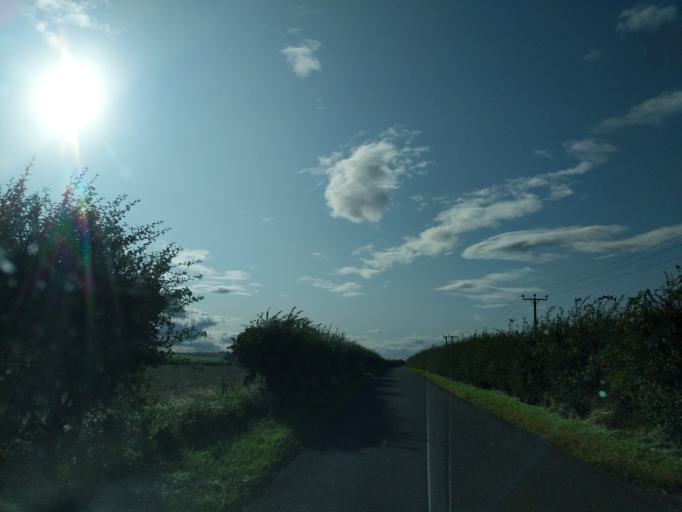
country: GB
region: Scotland
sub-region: East Lothian
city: Haddington
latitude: 55.9951
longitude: -2.7515
